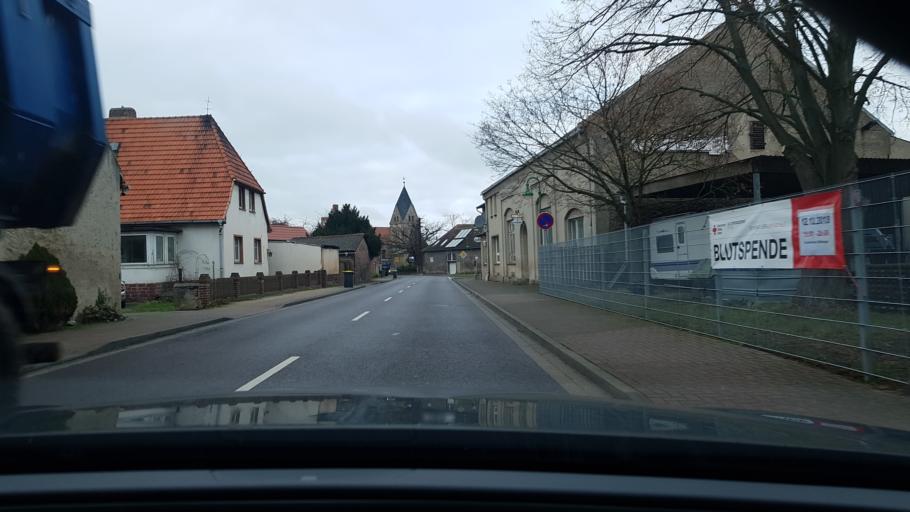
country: DE
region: Lower Saxony
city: Bahrdorf
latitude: 52.4138
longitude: 11.0725
